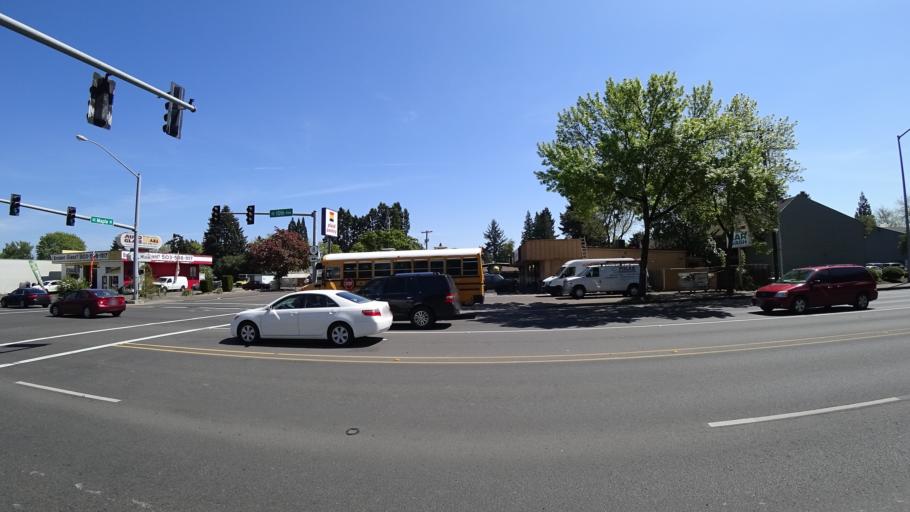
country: US
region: Oregon
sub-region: Washington County
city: Hillsboro
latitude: 45.5147
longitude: -122.9741
